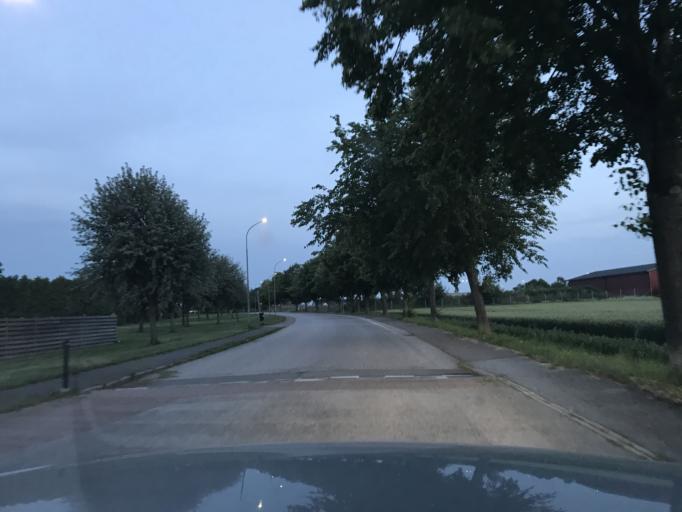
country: SE
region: Skane
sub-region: Svalovs Kommun
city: Svaloev
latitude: 55.9098
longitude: 13.0921
